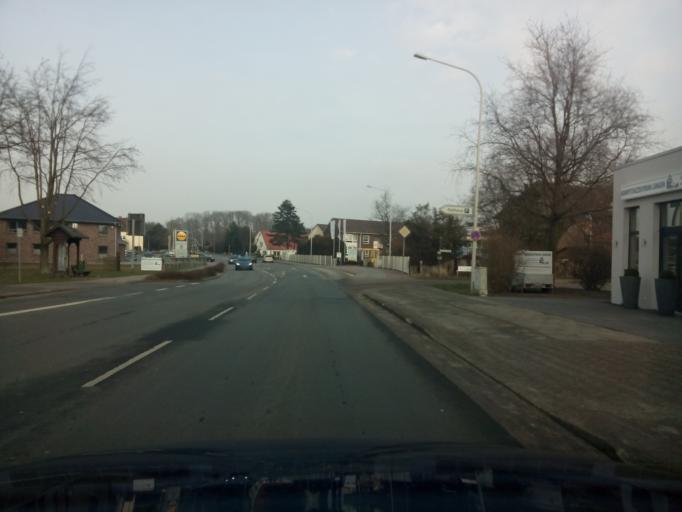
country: DE
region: Lower Saxony
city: Langen
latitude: 53.6091
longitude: 8.5950
